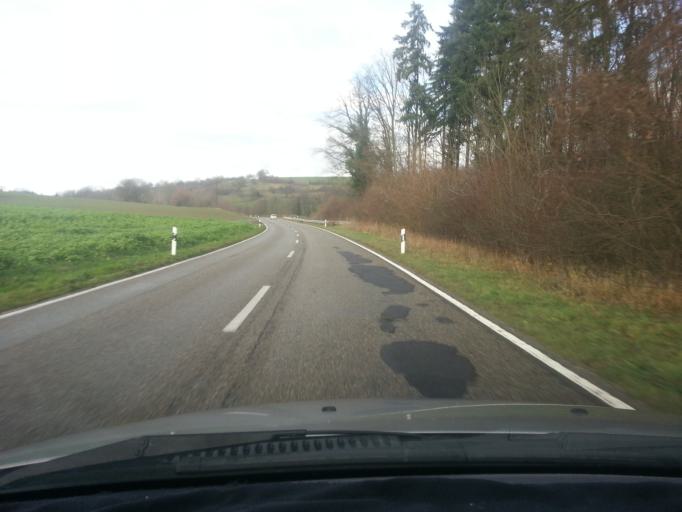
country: DE
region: Baden-Wuerttemberg
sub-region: Karlsruhe Region
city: Balzfeld
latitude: 49.1981
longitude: 8.8145
